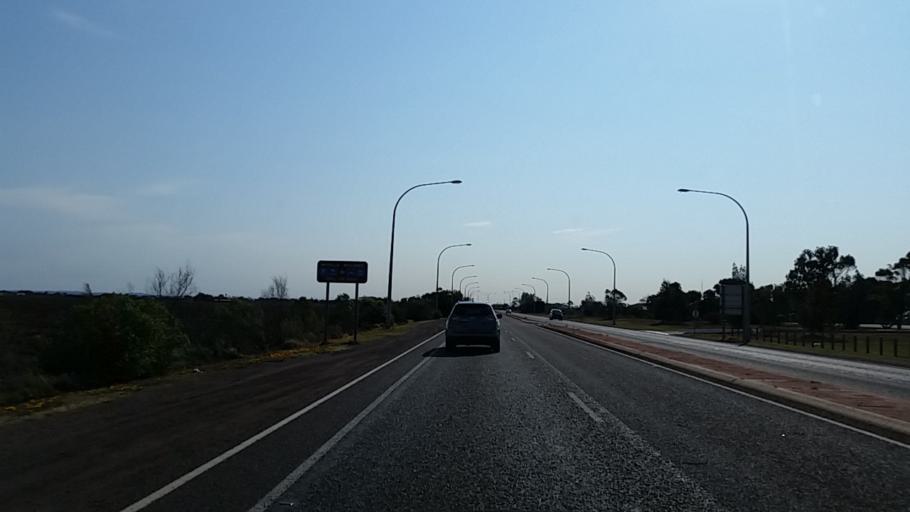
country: AU
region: South Australia
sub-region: Whyalla
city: Whyalla
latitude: -33.0403
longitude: 137.5612
